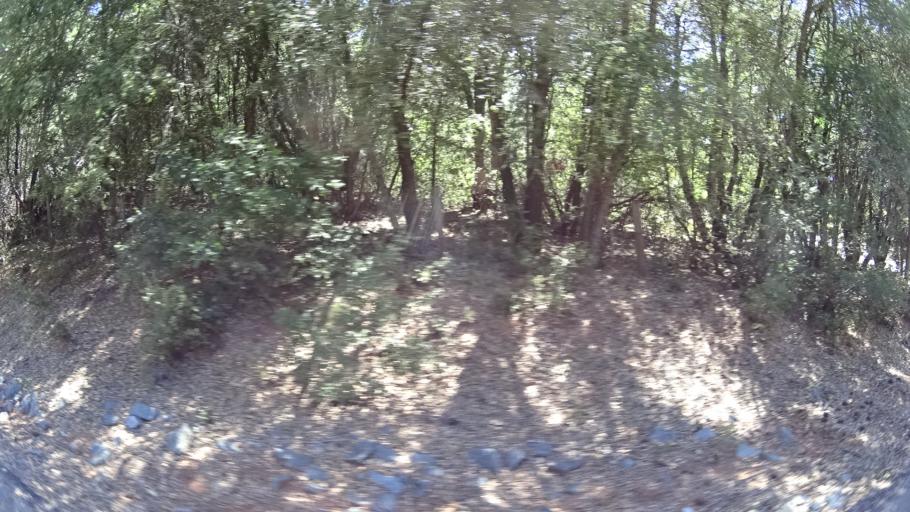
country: US
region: California
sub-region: Amador County
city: Pioneer
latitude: 38.3556
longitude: -120.5200
